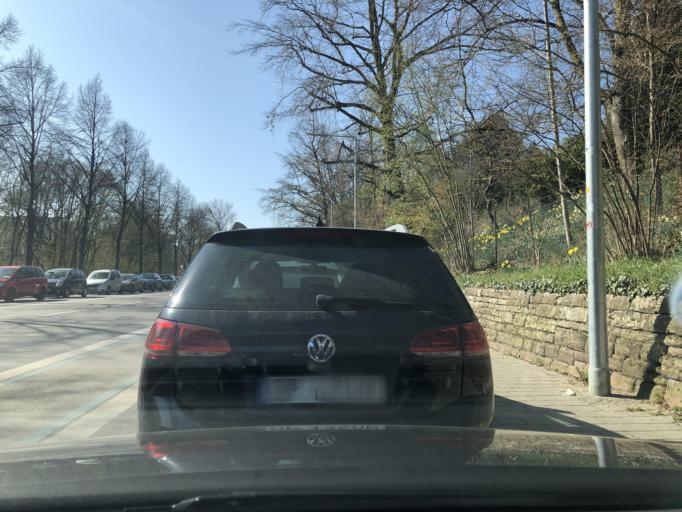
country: FR
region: Haute-Normandie
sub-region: Departement de la Seine-Maritime
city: Jumieges
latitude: 49.4133
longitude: 0.8333
